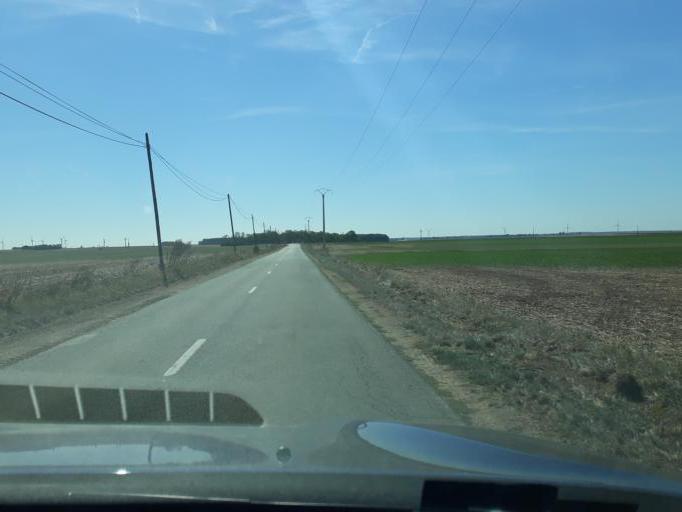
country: FR
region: Centre
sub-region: Departement du Loir-et-Cher
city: Ouzouer-le-Marche
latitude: 47.9384
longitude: 1.5187
